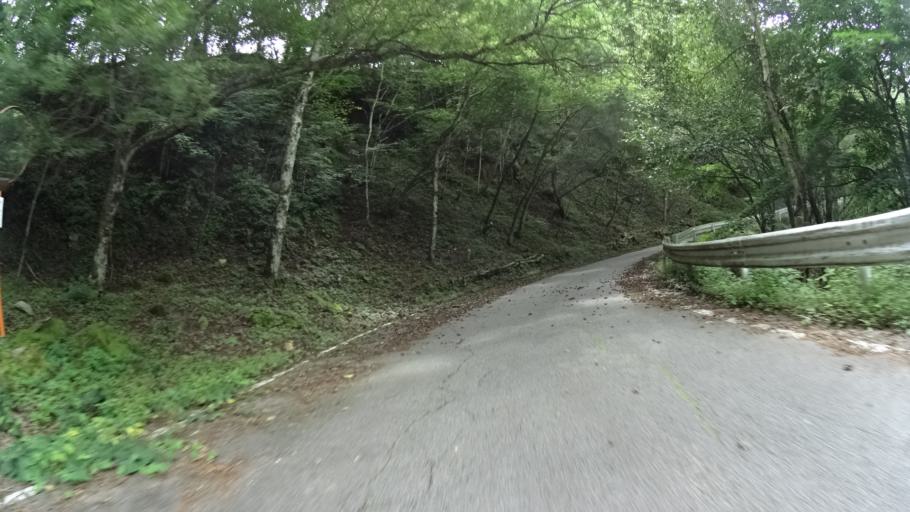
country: JP
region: Yamanashi
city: Kofu-shi
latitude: 35.8105
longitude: 138.5532
